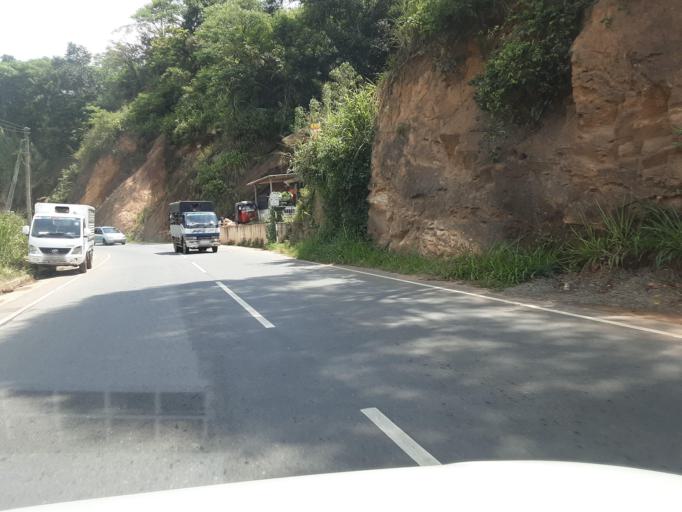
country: LK
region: Central
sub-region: Nuwara Eliya District
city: Nuwara Eliya
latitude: 6.9167
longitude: 80.9056
